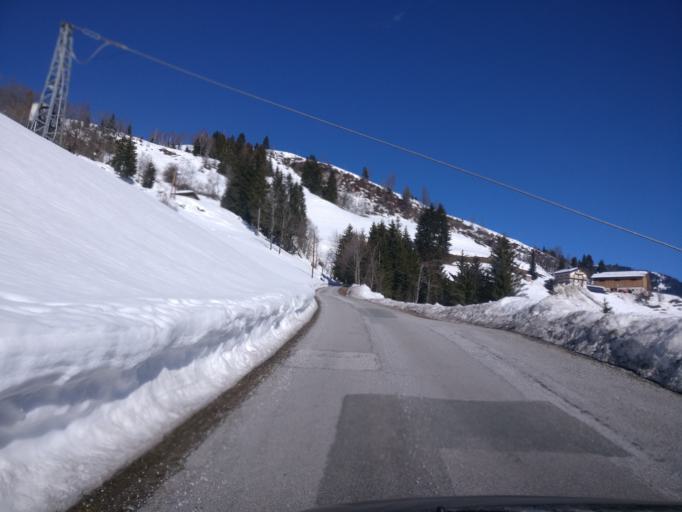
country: AT
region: Salzburg
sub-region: Politischer Bezirk Sankt Johann im Pongau
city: Wagrain
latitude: 47.3398
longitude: 13.2599
